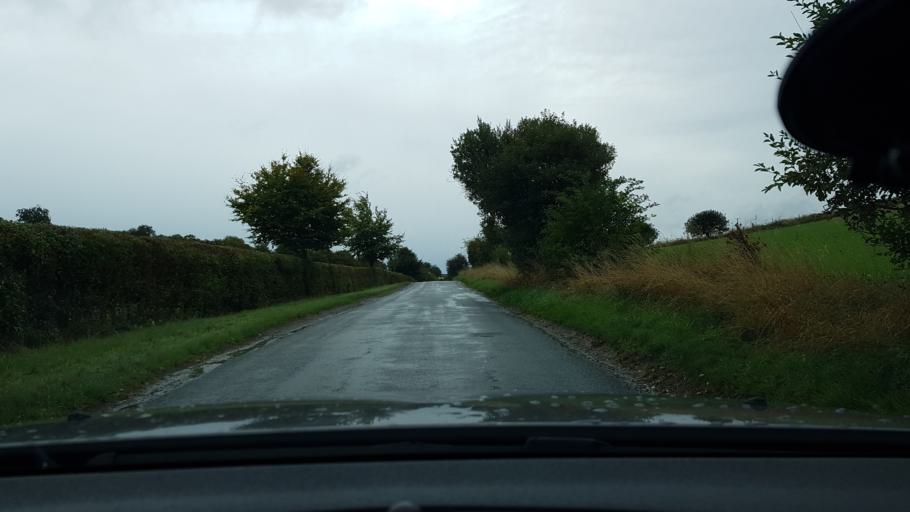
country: GB
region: England
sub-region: West Berkshire
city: Lambourn
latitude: 51.5327
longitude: -1.5268
